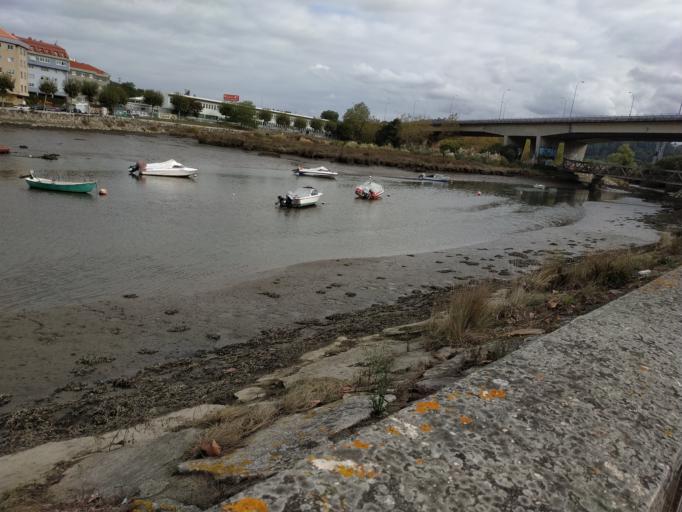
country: ES
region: Galicia
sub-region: Provincia da Coruna
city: Cambre
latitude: 43.3130
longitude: -8.3597
